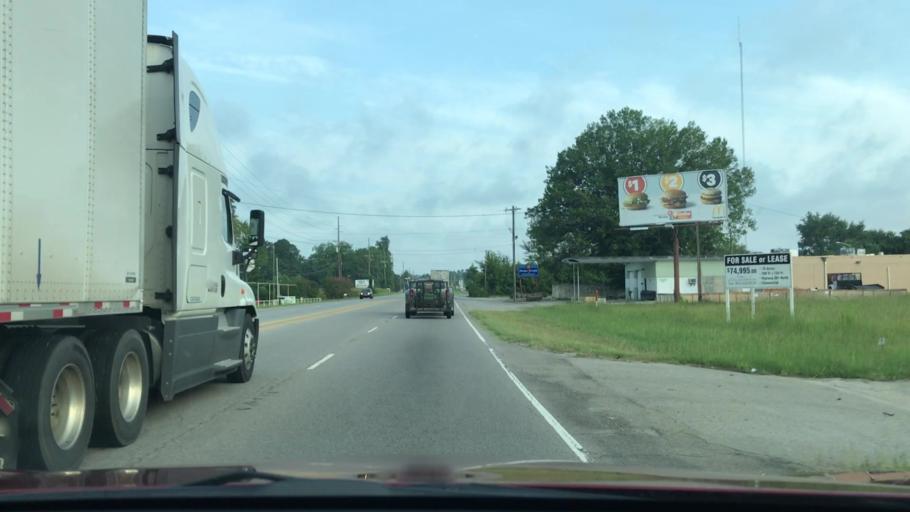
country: US
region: South Carolina
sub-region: Orangeburg County
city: Wilkinson Heights
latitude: 33.4824
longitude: -80.8258
